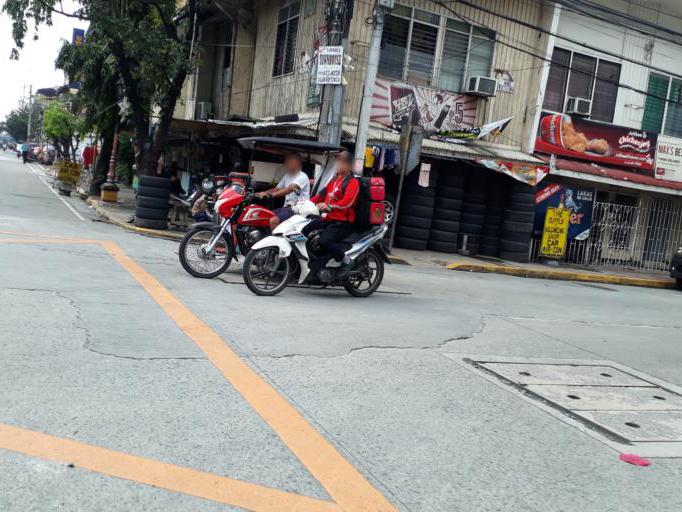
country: PH
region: Metro Manila
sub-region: City of Manila
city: Manila
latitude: 14.6165
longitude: 120.9960
